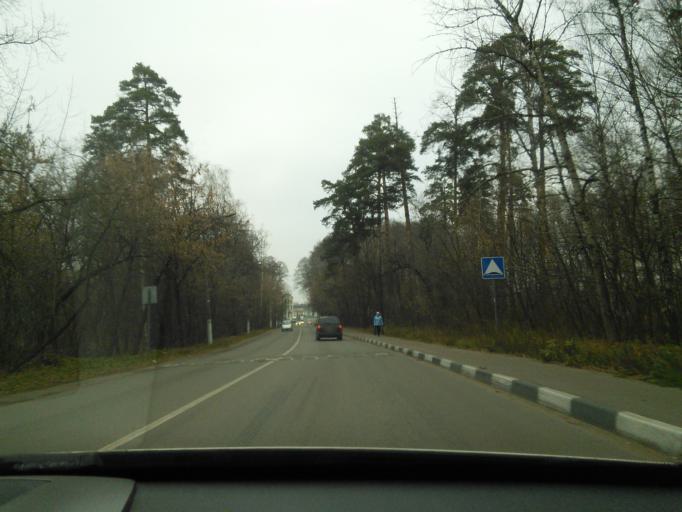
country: RU
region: Moskovskaya
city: Udel'naya
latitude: 55.6329
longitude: 38.0120
